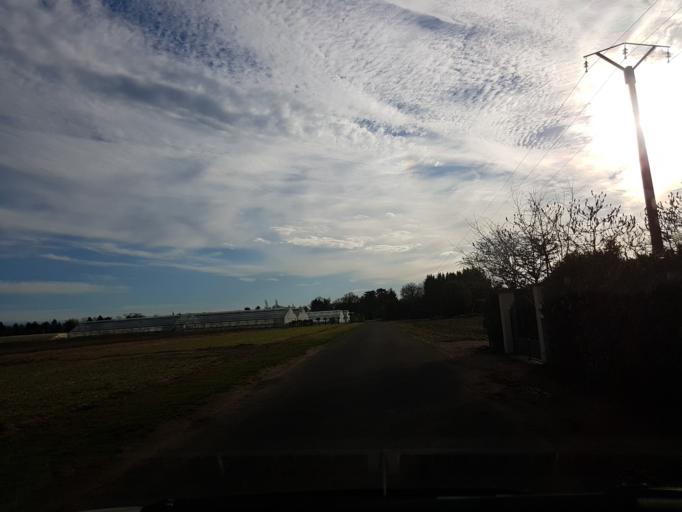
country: FR
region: Centre
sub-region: Departement du Loiret
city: Checy
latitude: 47.8860
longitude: 1.9946
